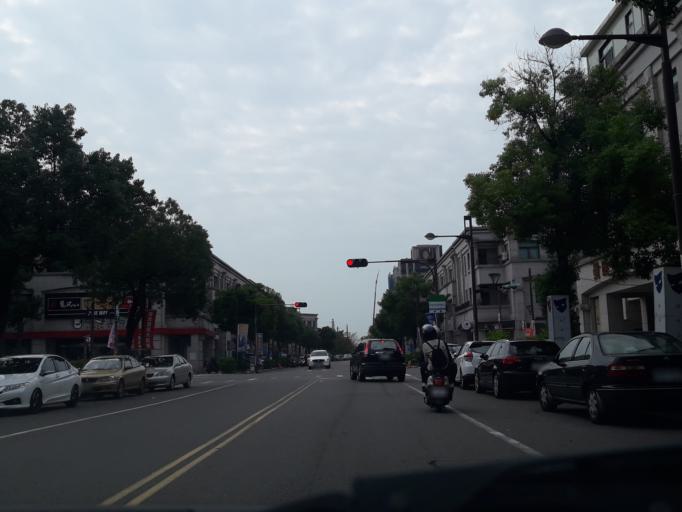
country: TW
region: Taiwan
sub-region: Hsinchu
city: Hsinchu
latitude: 24.6873
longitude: 120.9033
